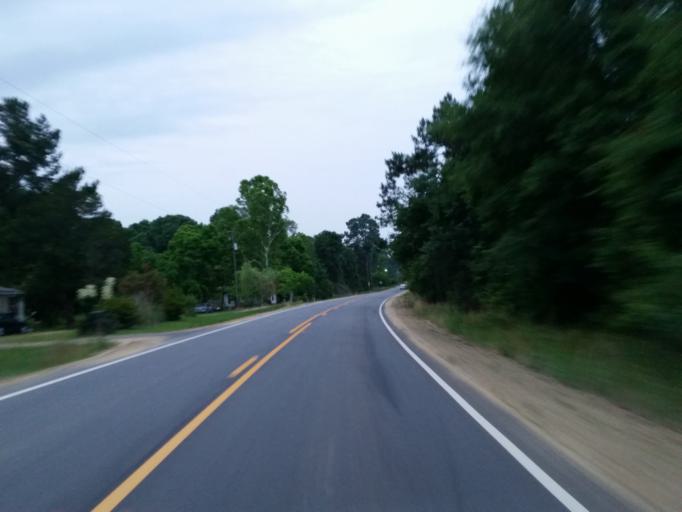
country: US
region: Georgia
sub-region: Turner County
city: Ashburn
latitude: 31.7666
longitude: -83.6863
